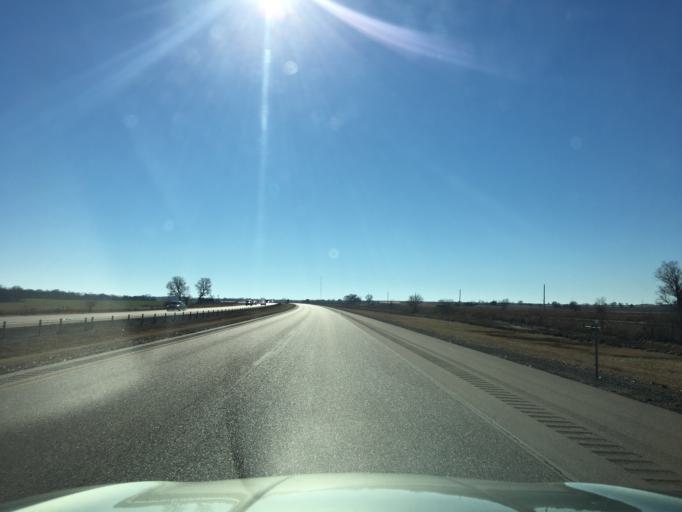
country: US
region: Oklahoma
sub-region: Kay County
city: Blackwell
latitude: 36.9025
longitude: -97.3540
